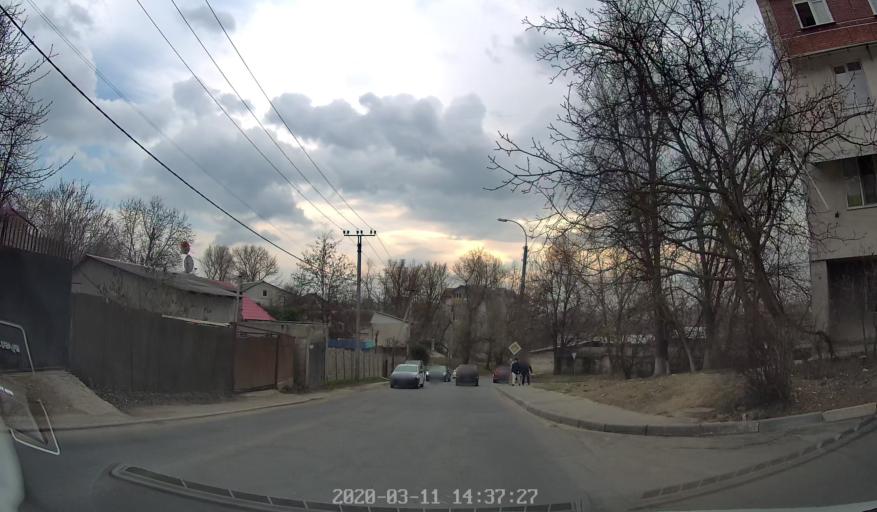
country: MD
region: Chisinau
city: Chisinau
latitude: 47.0217
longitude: 28.8753
